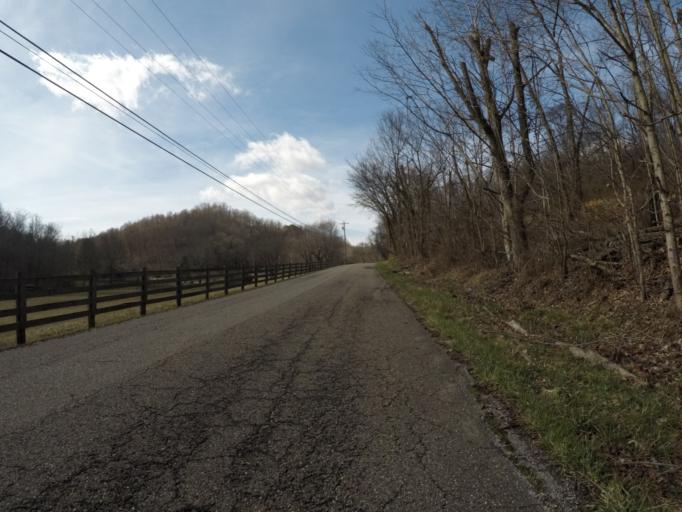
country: US
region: West Virginia
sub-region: Cabell County
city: Huntington
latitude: 38.4792
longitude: -82.4975
